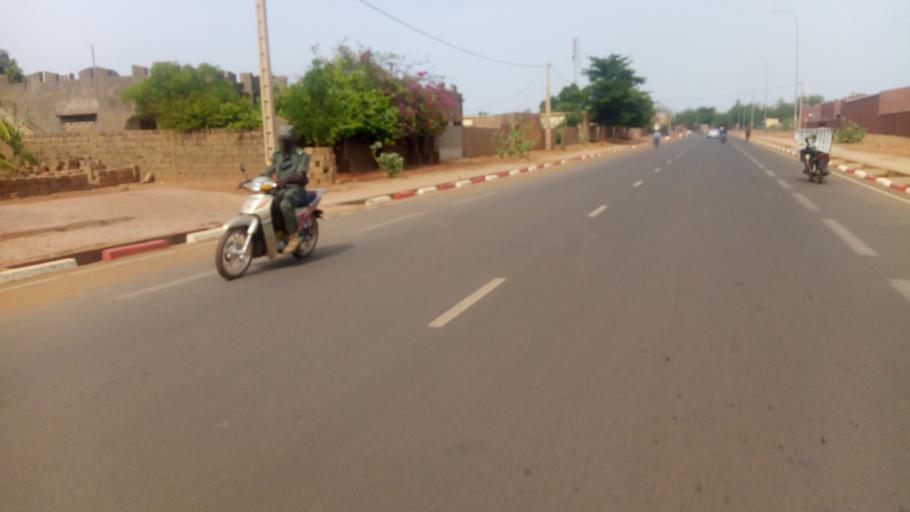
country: ML
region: Segou
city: Segou
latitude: 13.4281
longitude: -6.2848
